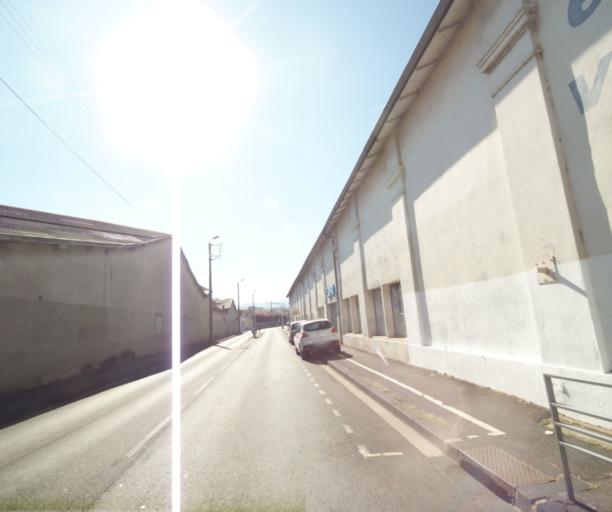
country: FR
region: Auvergne
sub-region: Departement du Puy-de-Dome
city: Clermont-Ferrand
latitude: 45.7830
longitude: 3.1131
